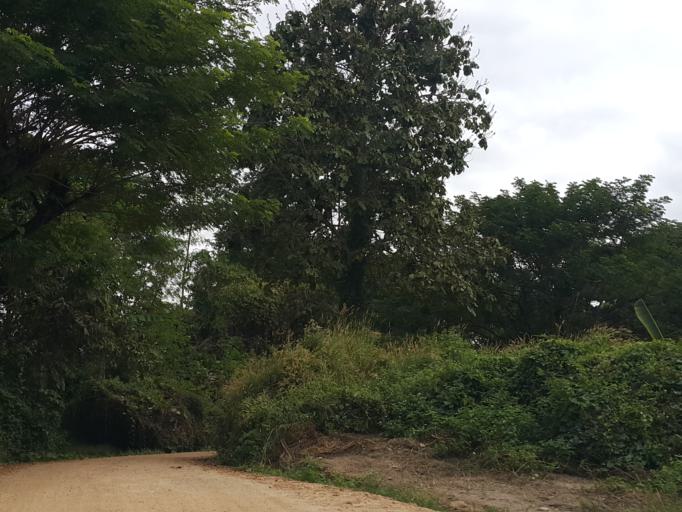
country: TH
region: Lampang
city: Hang Chat
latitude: 18.4760
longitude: 99.4106
